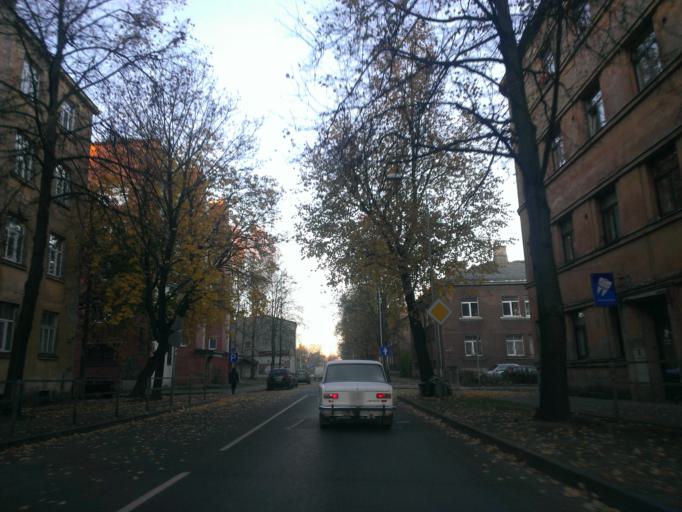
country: LV
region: Riga
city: Riga
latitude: 56.9763
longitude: 24.1437
